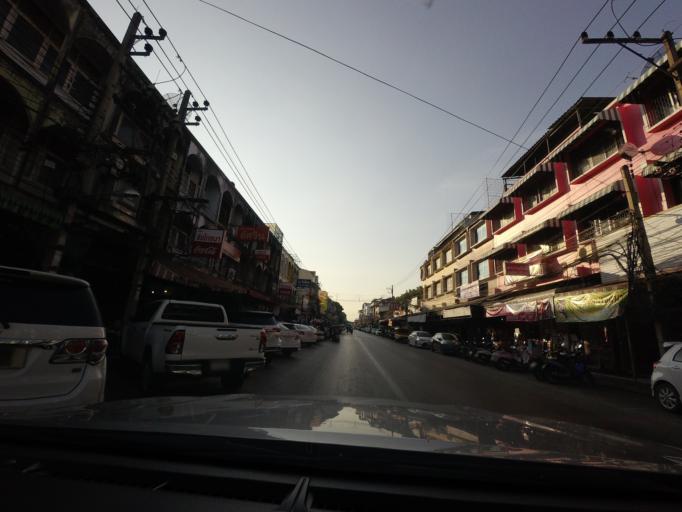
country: TH
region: Lampang
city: Lampang
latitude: 18.2892
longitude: 99.4877
